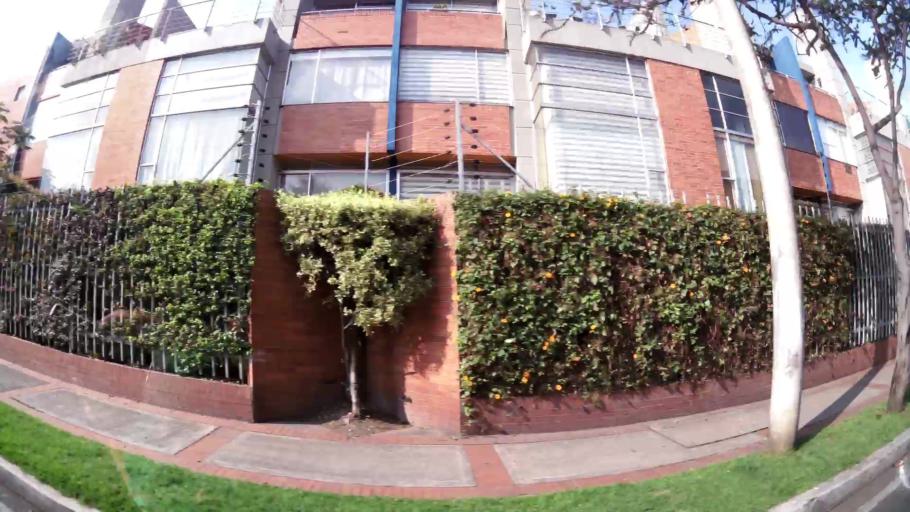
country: CO
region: Bogota D.C.
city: Barrio San Luis
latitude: 4.7319
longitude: -74.0621
